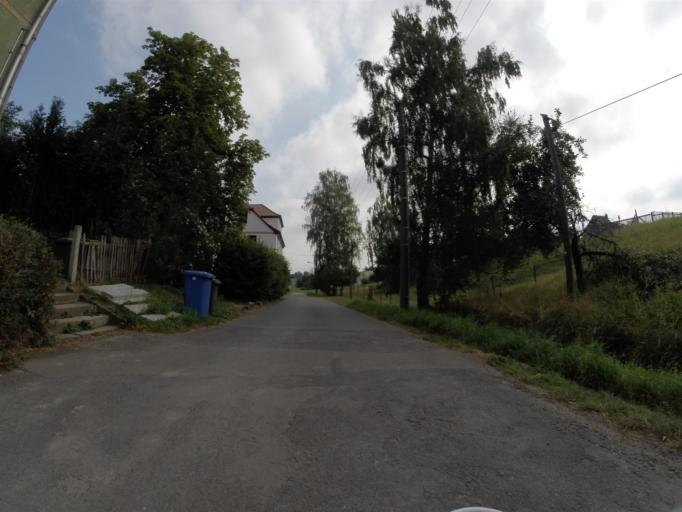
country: DE
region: Thuringia
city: Stadtroda
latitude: 50.8548
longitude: 11.7082
